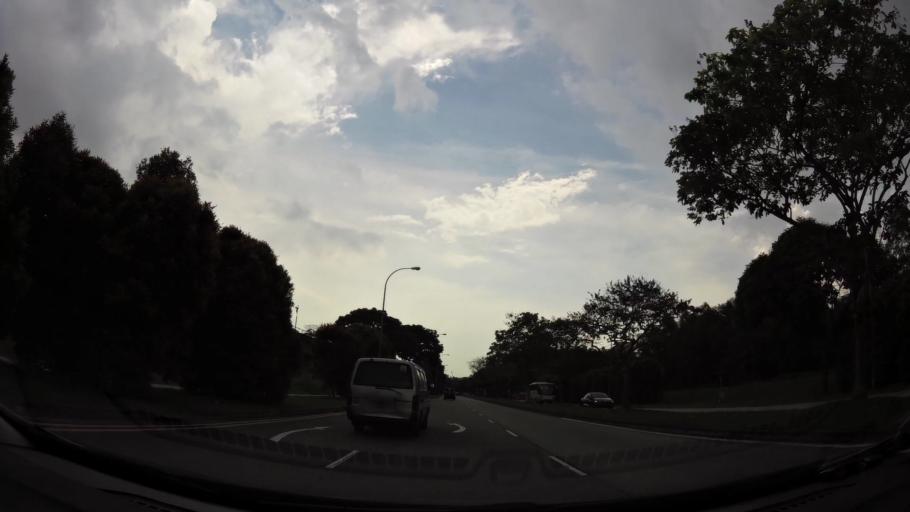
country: SG
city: Singapore
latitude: 1.3638
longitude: 103.9453
